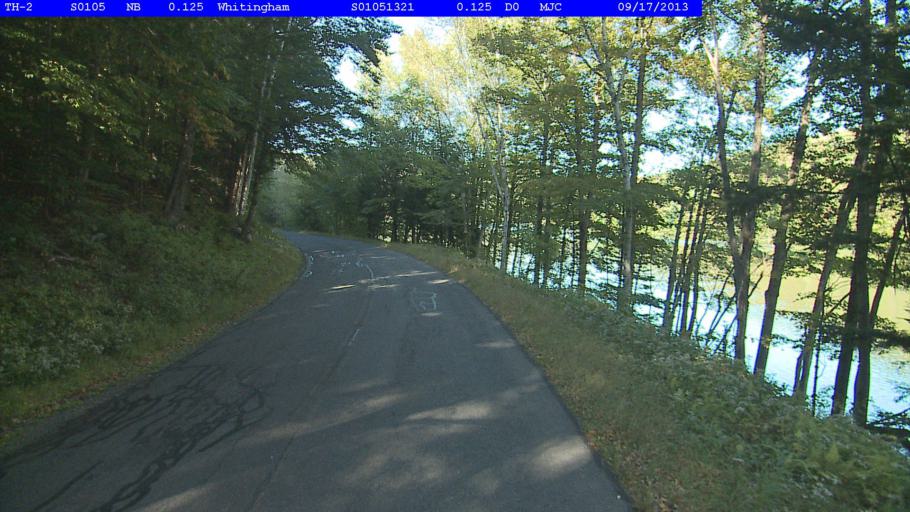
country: US
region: Massachusetts
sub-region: Franklin County
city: Charlemont
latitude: 42.7408
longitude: -72.9277
